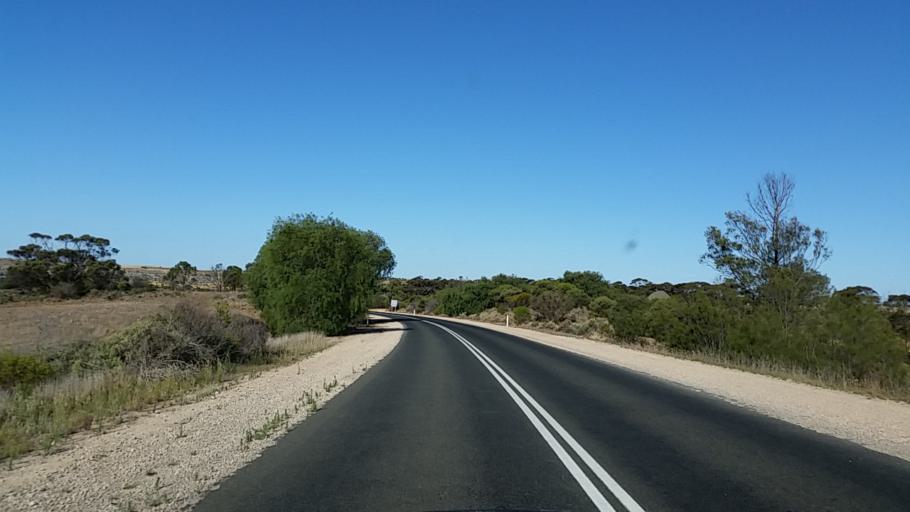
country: AU
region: South Australia
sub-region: Mid Murray
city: Mannum
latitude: -34.7576
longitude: 139.5515
